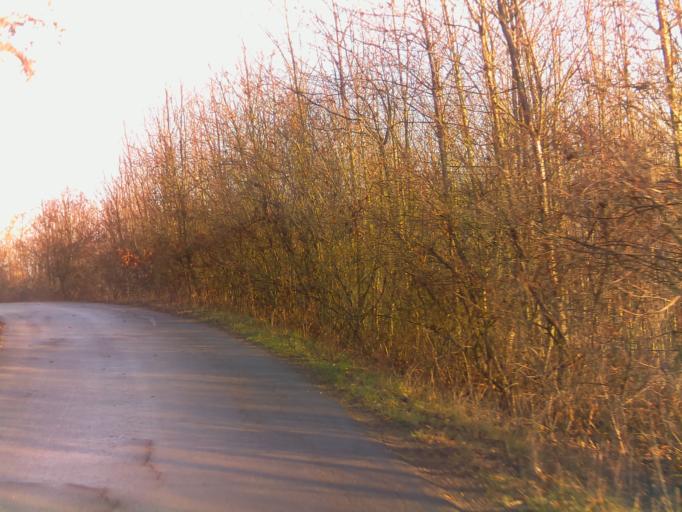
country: DE
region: Thuringia
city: Gumperda
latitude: 50.7956
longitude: 11.5148
